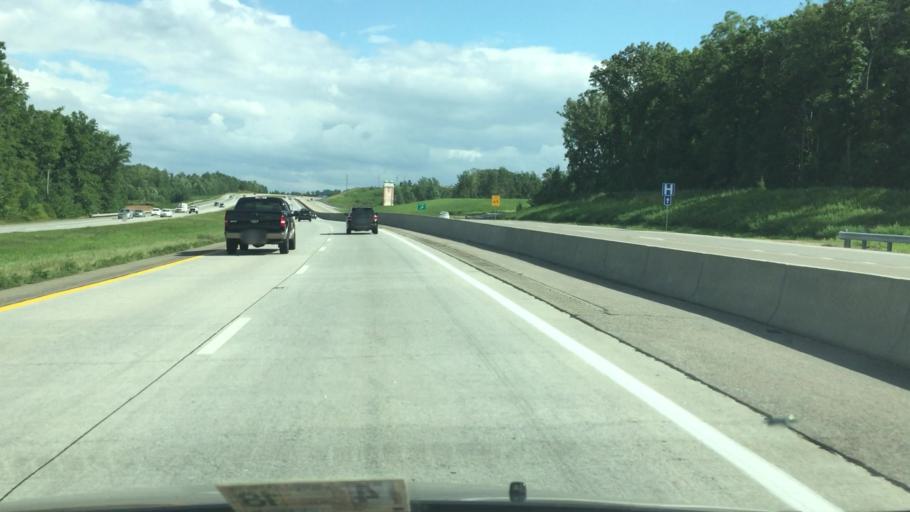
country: US
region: Virginia
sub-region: Chesterfield County
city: Brandermill
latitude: 37.5235
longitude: -77.6937
